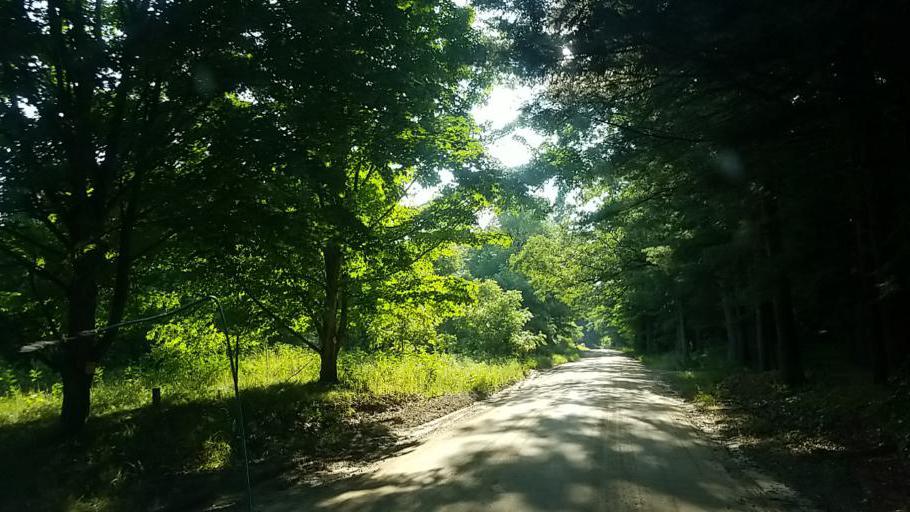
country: US
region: Michigan
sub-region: Newaygo County
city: Newaygo
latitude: 43.3800
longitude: -85.8384
